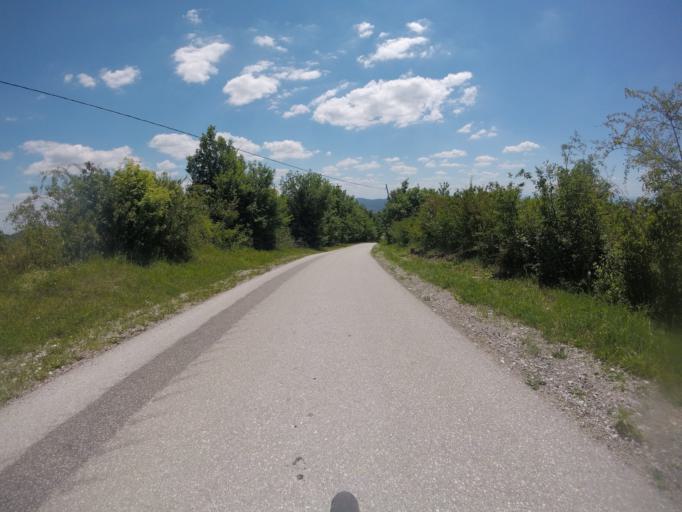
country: SI
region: Metlika
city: Metlika
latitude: 45.6981
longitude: 15.3869
